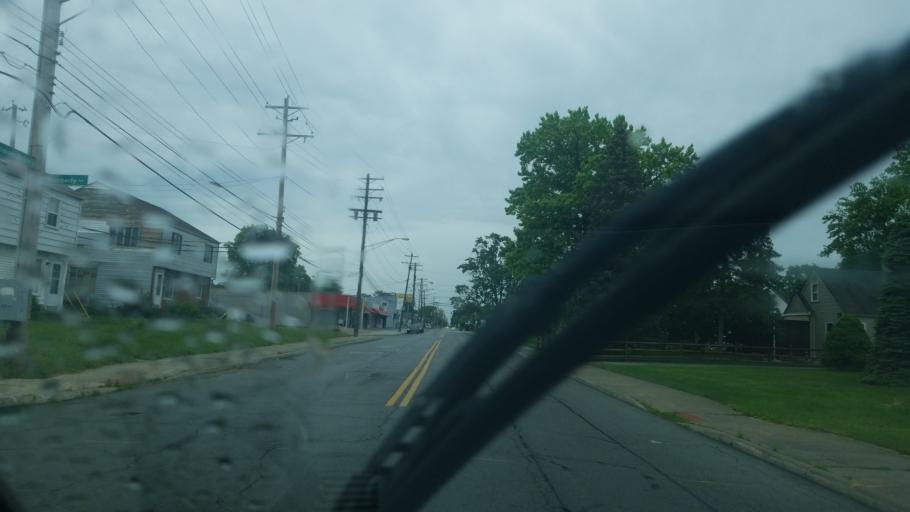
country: US
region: Ohio
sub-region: Franklin County
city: Minerva Park
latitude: 40.0327
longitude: -82.9925
